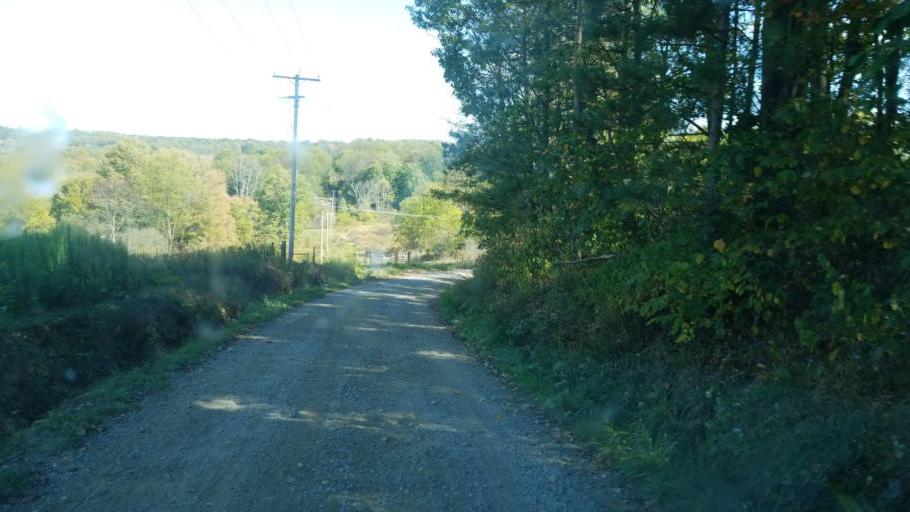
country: US
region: Pennsylvania
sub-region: Mercer County
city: Mercer
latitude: 41.3291
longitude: -80.2537
